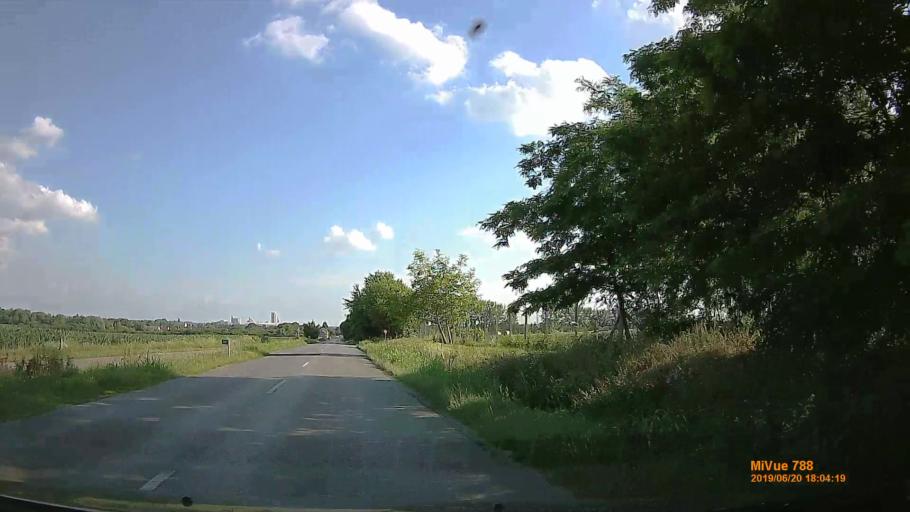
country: HU
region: Baranya
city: Szentlorinc
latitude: 46.0520
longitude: 17.9885
